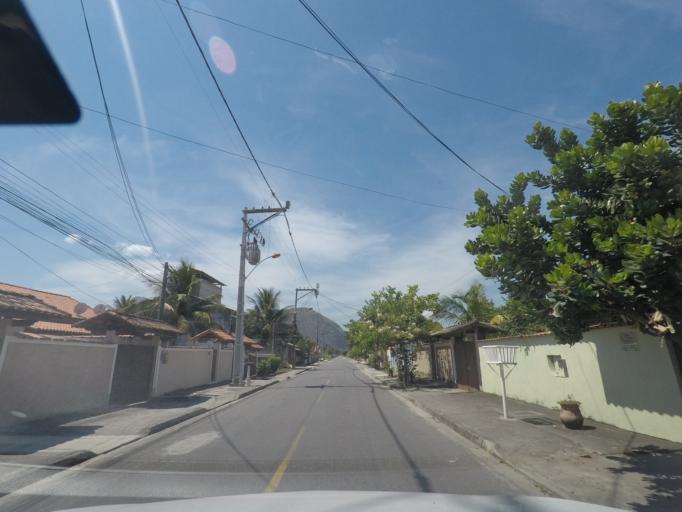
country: BR
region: Rio de Janeiro
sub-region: Marica
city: Marica
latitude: -22.9632
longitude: -42.9585
